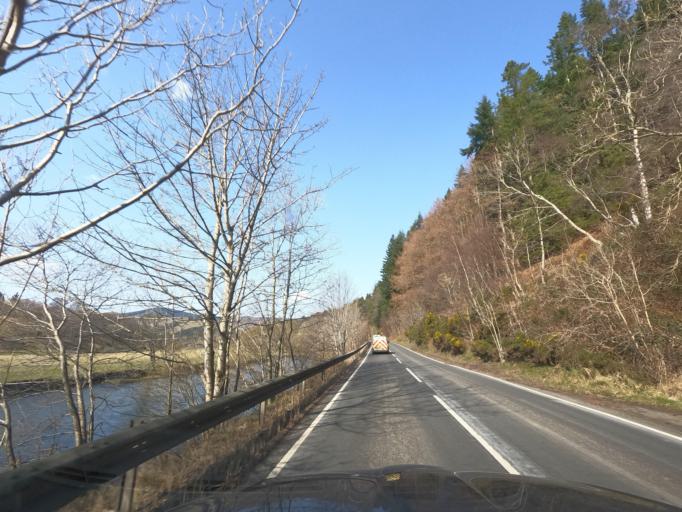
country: GB
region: Scotland
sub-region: The Scottish Borders
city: Innerleithen
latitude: 55.6234
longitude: -2.9583
